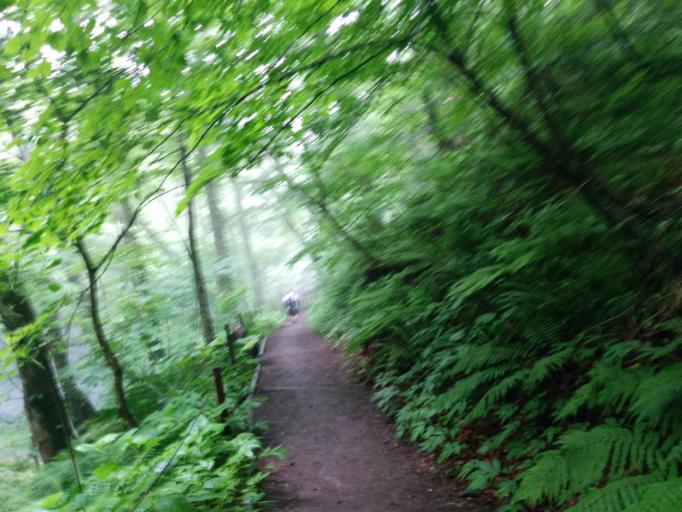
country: JP
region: Akita
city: Noshiromachi
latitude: 40.5634
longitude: 139.9792
